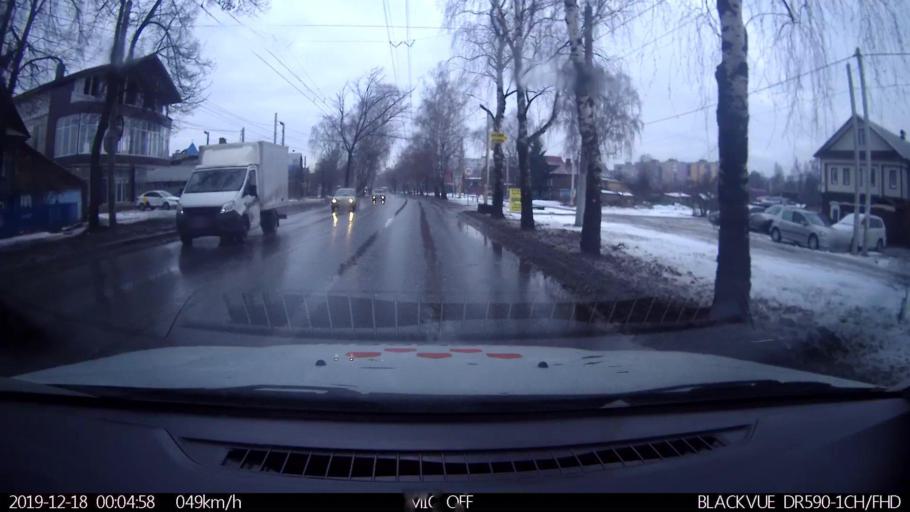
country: RU
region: Nizjnij Novgorod
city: Neklyudovo
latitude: 56.3652
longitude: 43.8492
